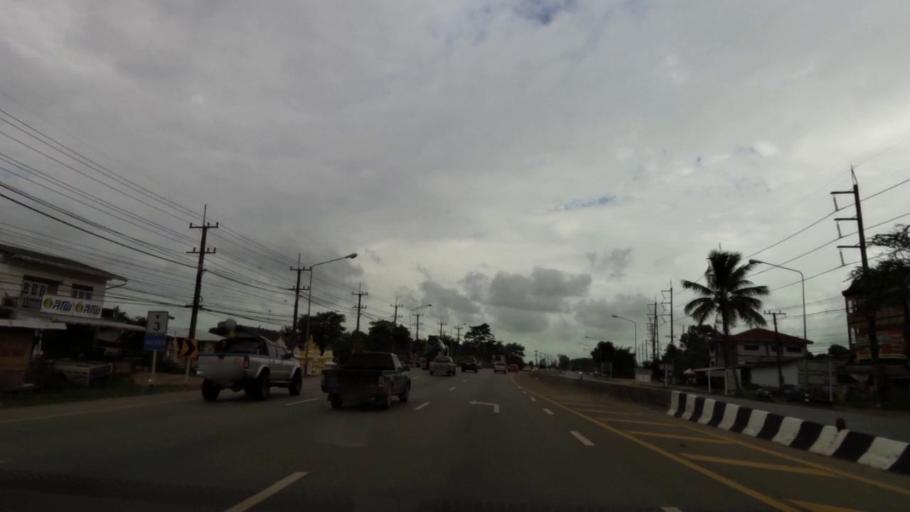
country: TH
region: Chanthaburi
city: Tha Mai
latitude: 12.7223
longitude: 101.9577
